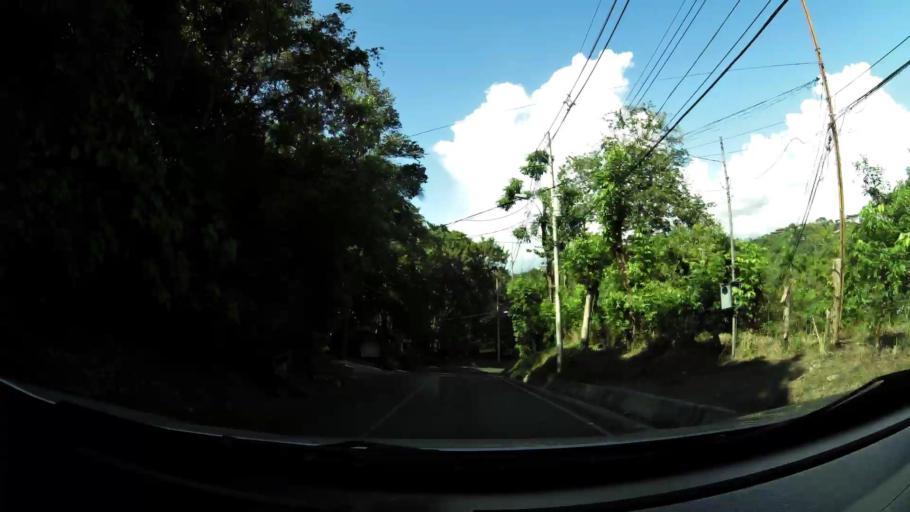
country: CR
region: Puntarenas
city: Quepos
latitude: 9.4132
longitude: -84.1558
